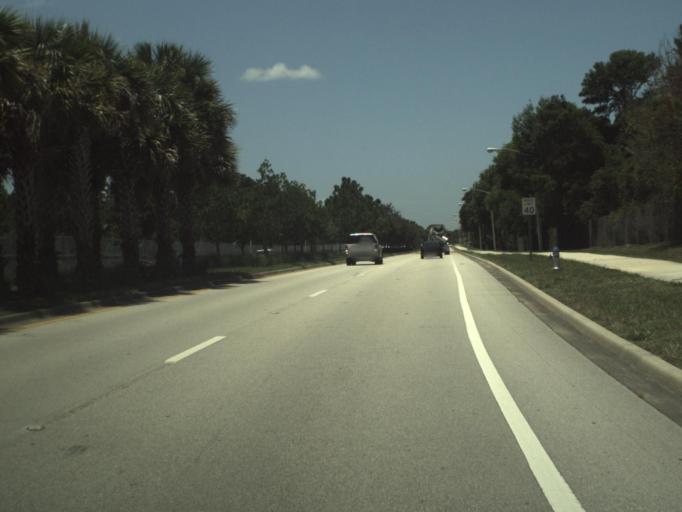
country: US
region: Florida
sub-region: Martin County
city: Sewall's Point
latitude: 27.1854
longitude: -80.2255
